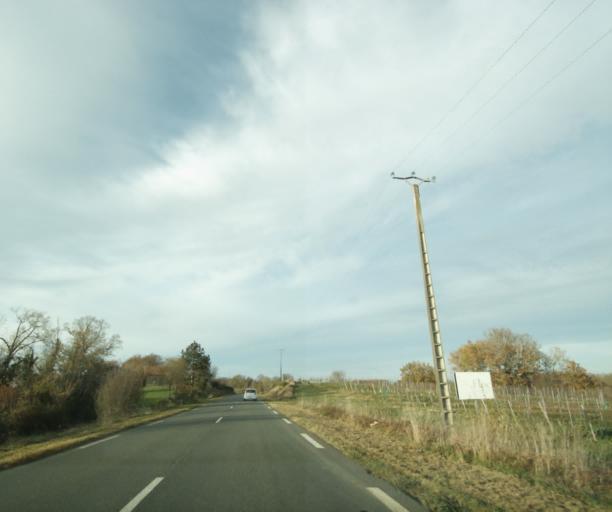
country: FR
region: Midi-Pyrenees
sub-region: Departement du Gers
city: Eauze
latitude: 43.7950
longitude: 0.0998
